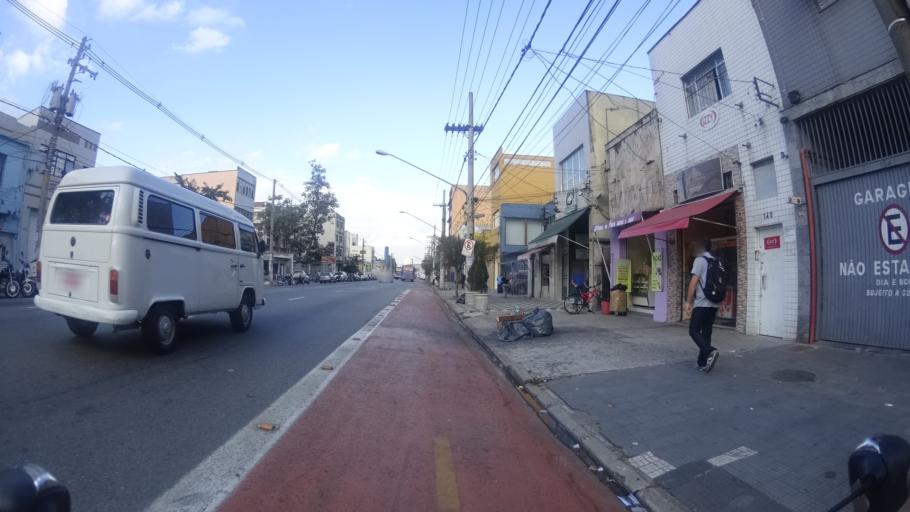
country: BR
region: Sao Paulo
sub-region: Sao Paulo
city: Sao Paulo
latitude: -23.5254
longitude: -46.6277
